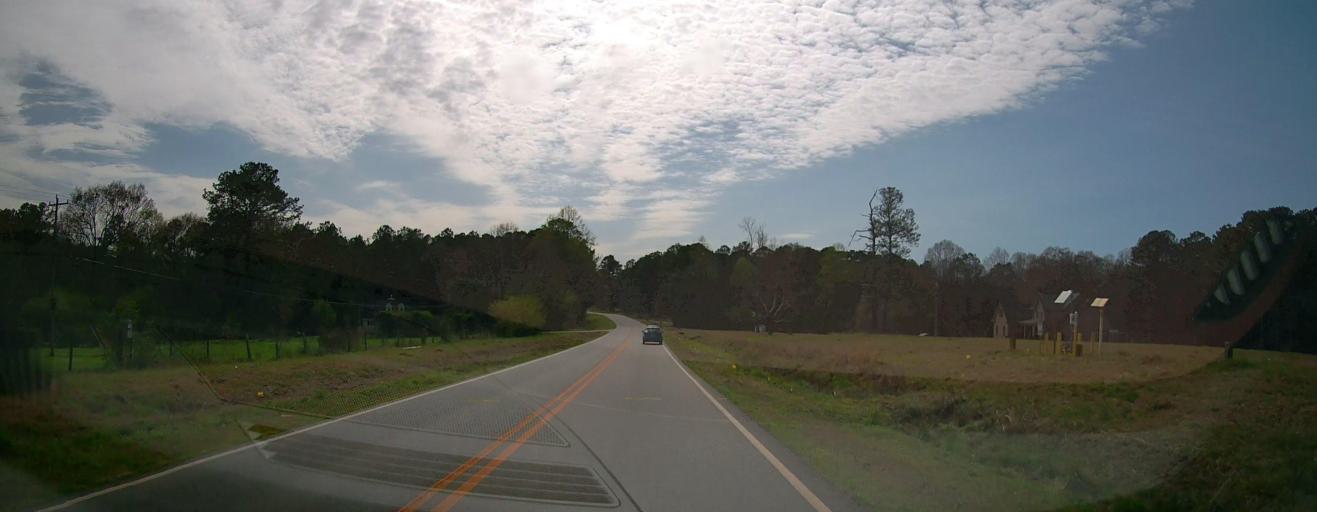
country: US
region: Georgia
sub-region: Monroe County
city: Forsyth
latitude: 33.0535
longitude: -83.8930
